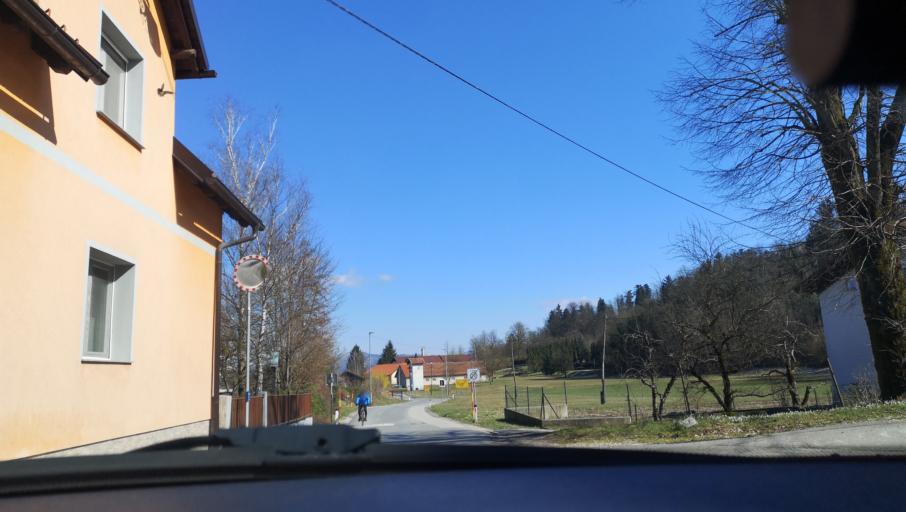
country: SI
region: Ig
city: Ig
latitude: 45.9587
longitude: 14.5152
